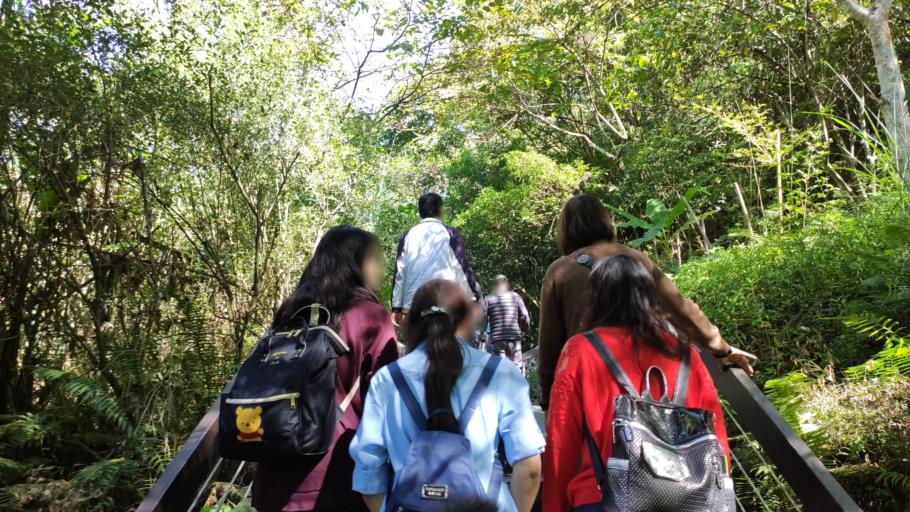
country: TW
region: Taiwan
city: Daxi
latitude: 24.8354
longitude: 121.3025
